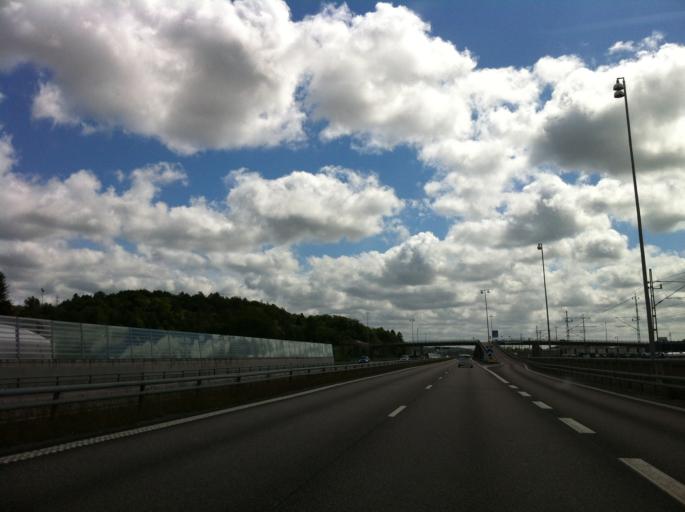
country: SE
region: Vaestra Goetaland
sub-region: Ale Kommun
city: Surte
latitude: 57.8700
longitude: 12.0281
